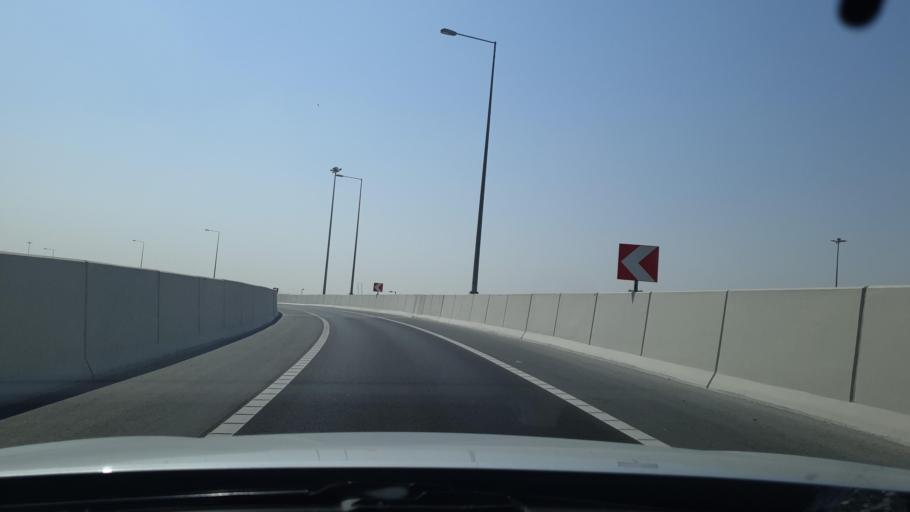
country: QA
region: Baladiyat ad Dawhah
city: Doha
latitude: 25.2216
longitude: 51.5322
